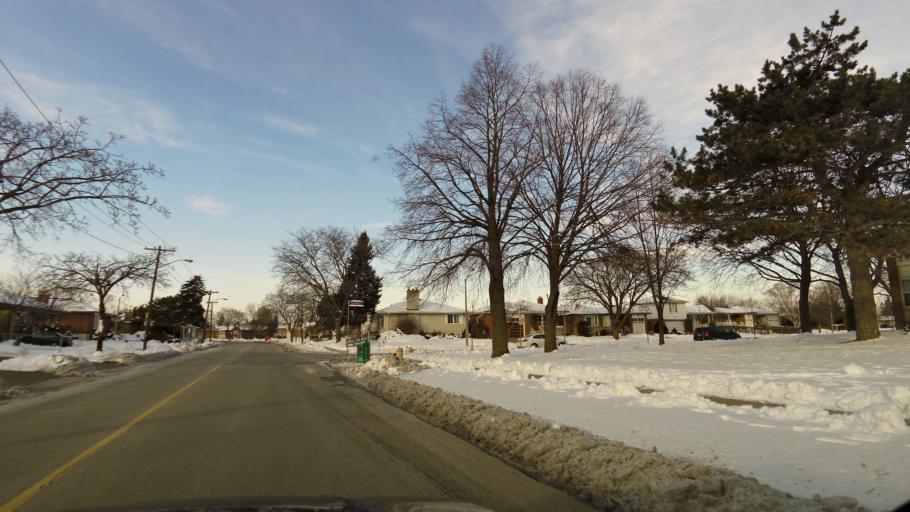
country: CA
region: Ontario
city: Etobicoke
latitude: 43.6566
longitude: -79.5772
